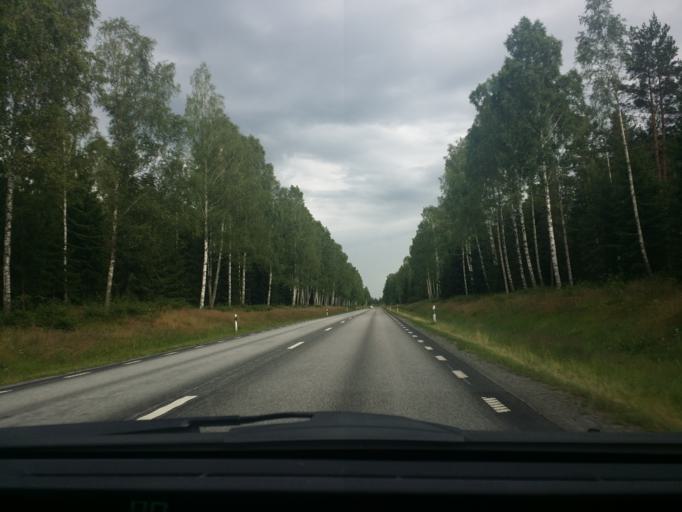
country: SE
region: OErebro
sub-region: Nora Kommun
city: Nora
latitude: 59.4837
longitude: 15.0763
